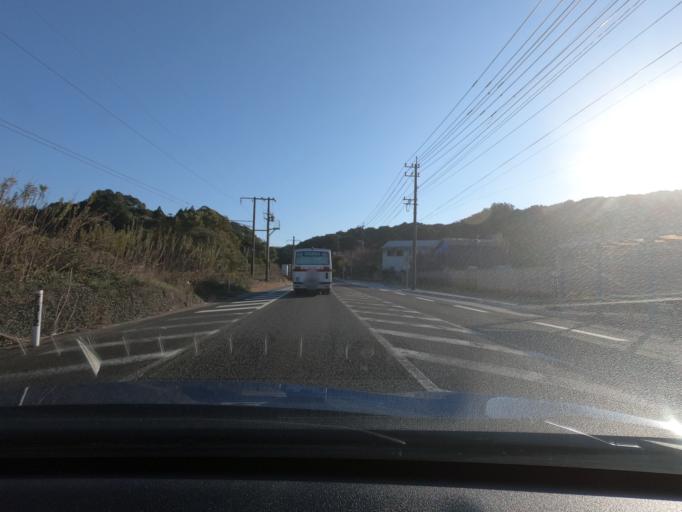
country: JP
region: Kagoshima
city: Akune
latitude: 32.0003
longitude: 130.1960
